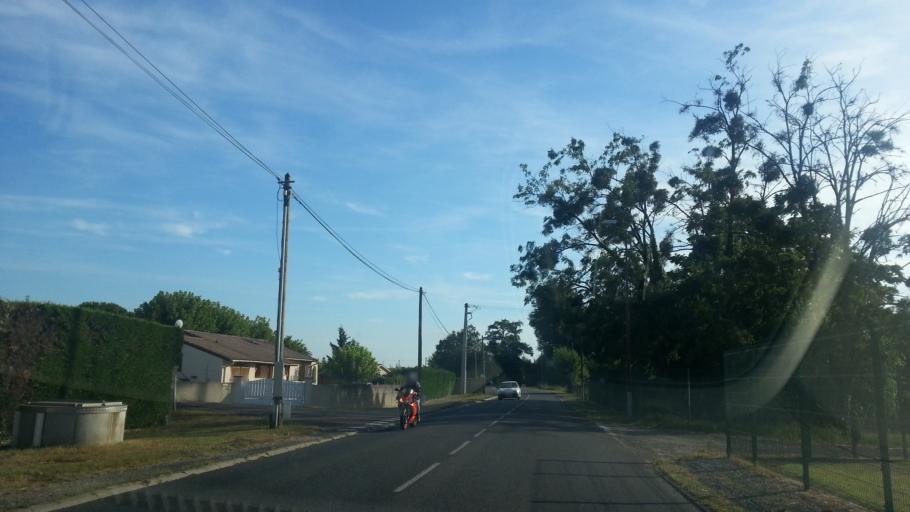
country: FR
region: Aquitaine
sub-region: Departement de la Gironde
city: Podensac
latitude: 44.6457
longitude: -0.3577
